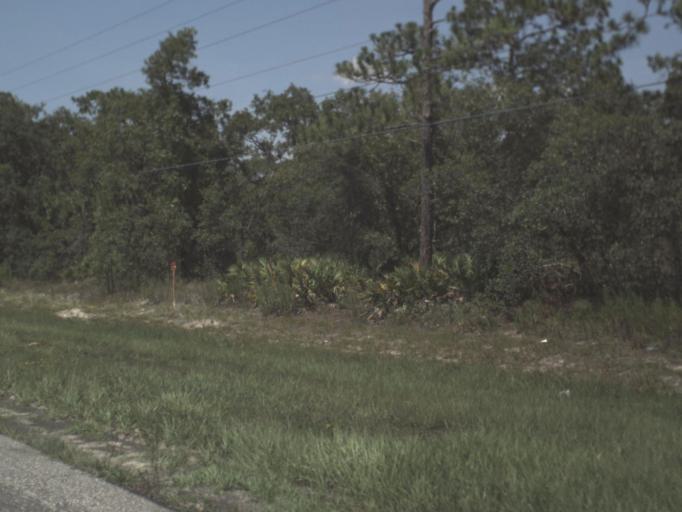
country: US
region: Florida
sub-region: Hernando County
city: North Weeki Wachee
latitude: 28.6320
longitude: -82.5518
